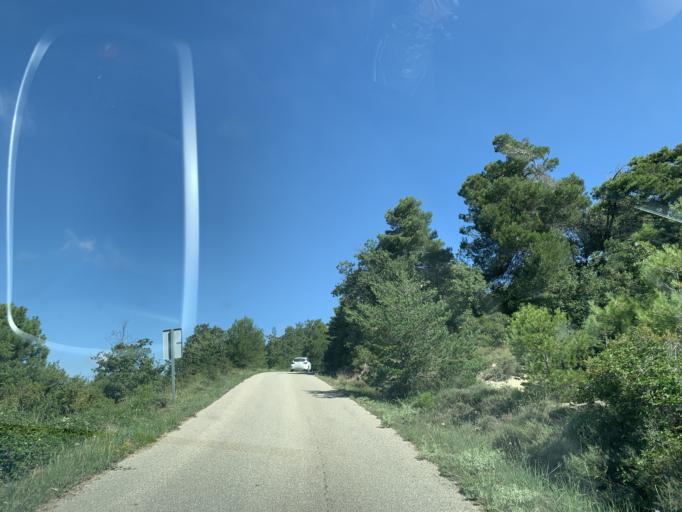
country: ES
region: Catalonia
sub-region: Provincia de Tarragona
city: Conesa
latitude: 41.5398
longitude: 1.2870
